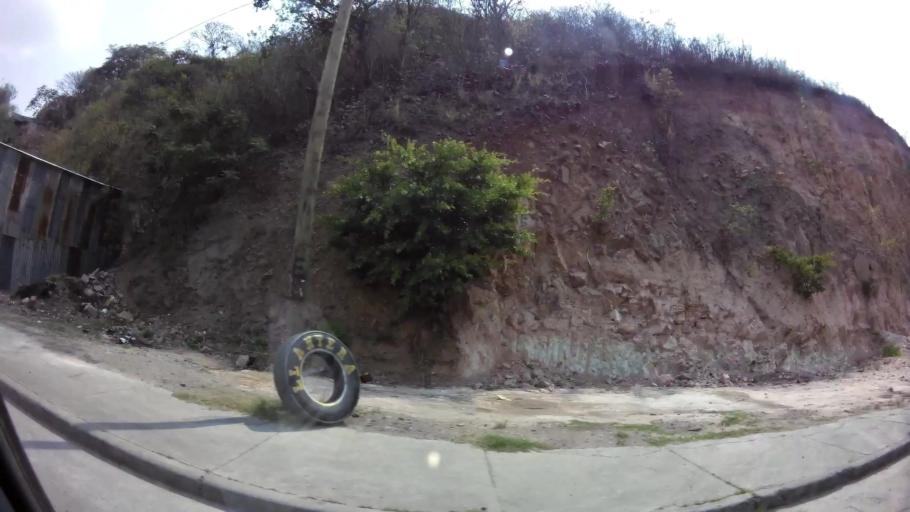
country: HN
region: Francisco Morazan
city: Tegucigalpa
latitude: 14.1125
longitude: -87.2129
